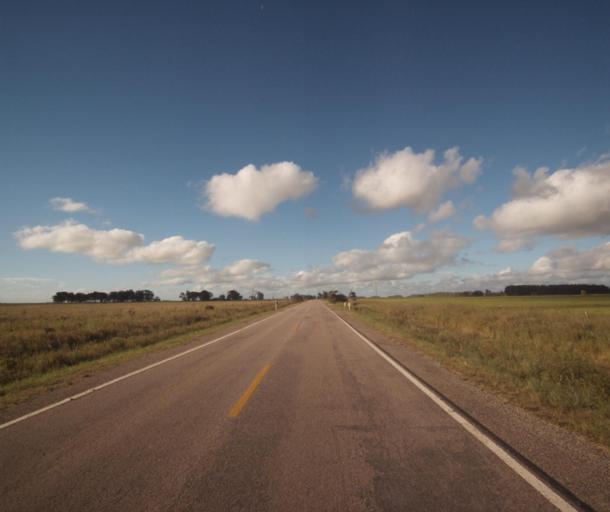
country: BR
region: Rio Grande do Sul
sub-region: Arroio Grande
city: Arroio Grande
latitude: -32.4504
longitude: -52.5704
